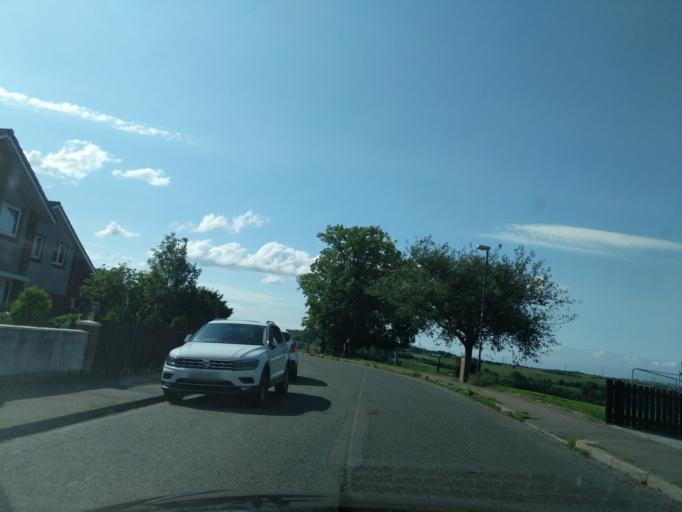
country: GB
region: Scotland
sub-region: Midlothian
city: Bonnyrigg
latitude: 55.8722
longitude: -3.1268
